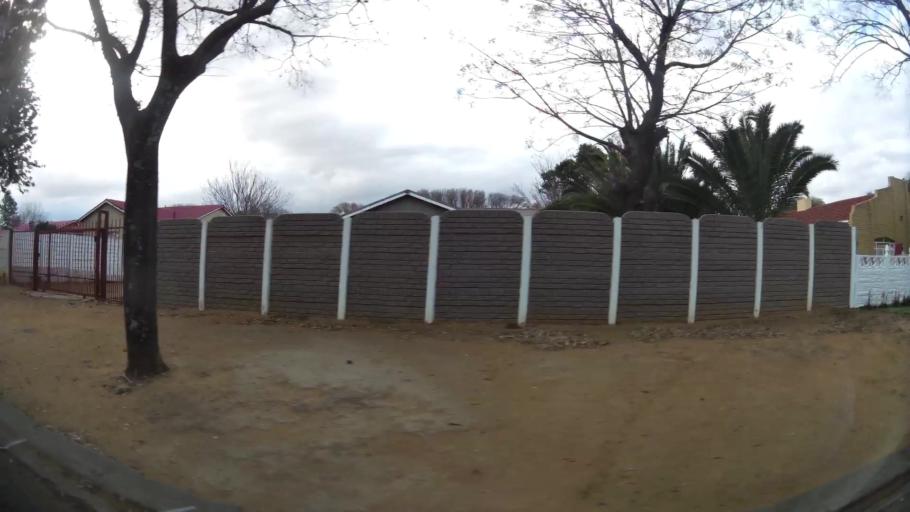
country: ZA
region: Orange Free State
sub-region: Lejweleputswa District Municipality
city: Welkom
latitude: -27.9805
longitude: 26.7226
